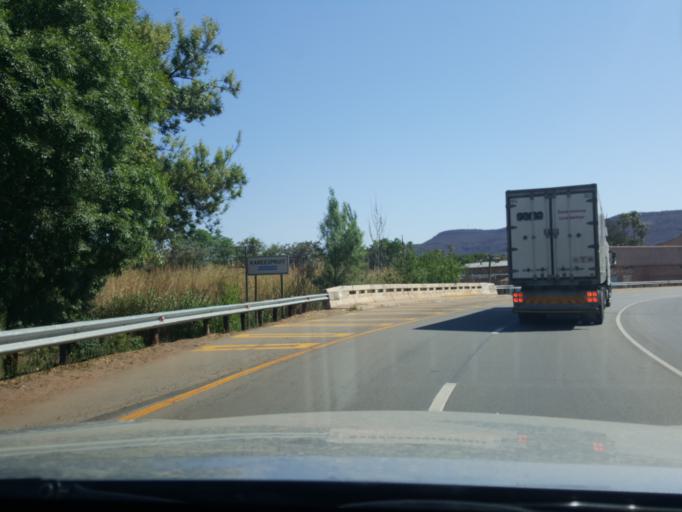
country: ZA
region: North-West
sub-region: Ngaka Modiri Molema District Municipality
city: Zeerust
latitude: -25.5473
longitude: 26.0732
